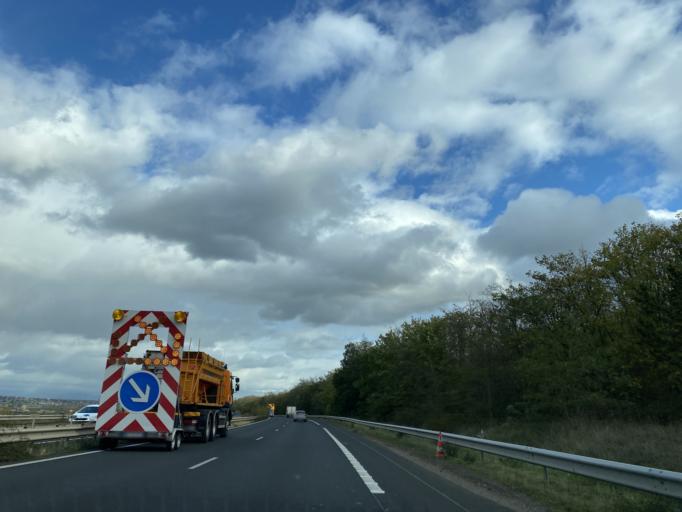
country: FR
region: Auvergne
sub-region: Departement du Puy-de-Dome
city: Aulnat
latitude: 45.7732
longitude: 3.1659
